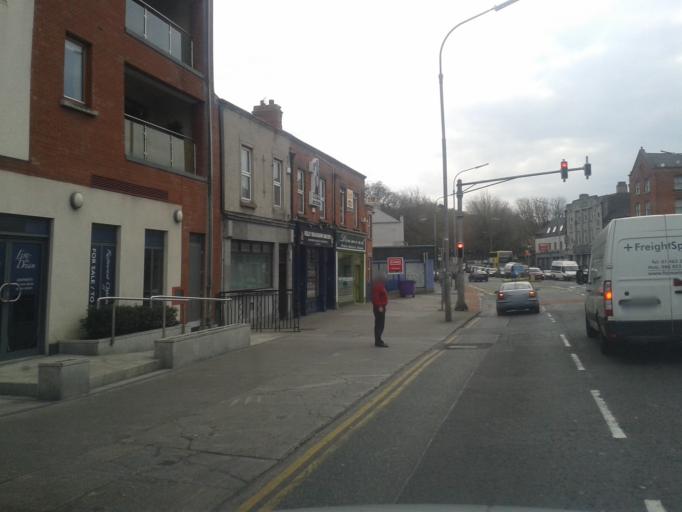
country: IE
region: Leinster
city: Drumcondra
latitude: 53.3682
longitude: -6.2551
